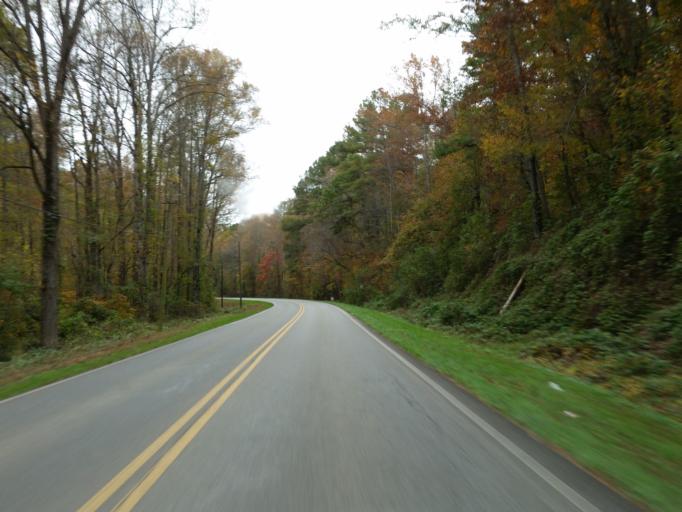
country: US
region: Georgia
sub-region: Pickens County
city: Jasper
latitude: 34.4876
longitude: -84.4220
